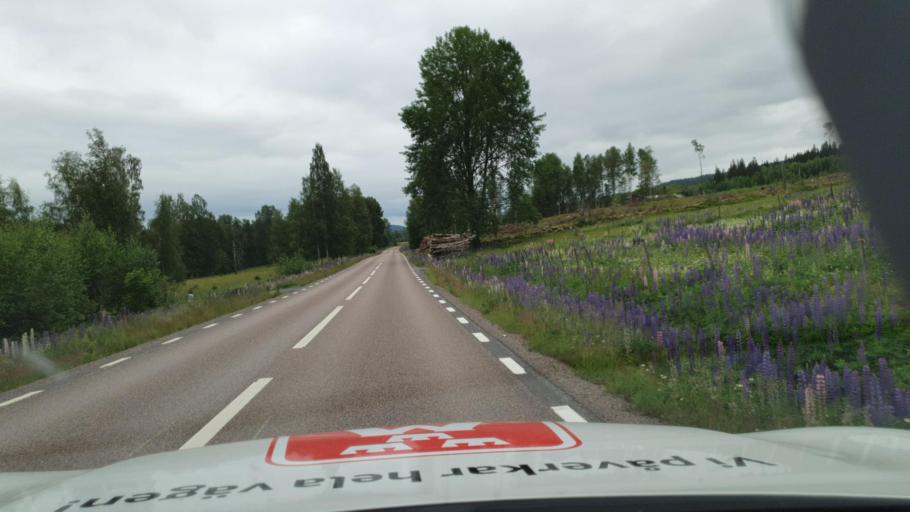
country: SE
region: Vaermland
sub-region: Sunne Kommun
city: Sunne
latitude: 59.9014
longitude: 12.9104
